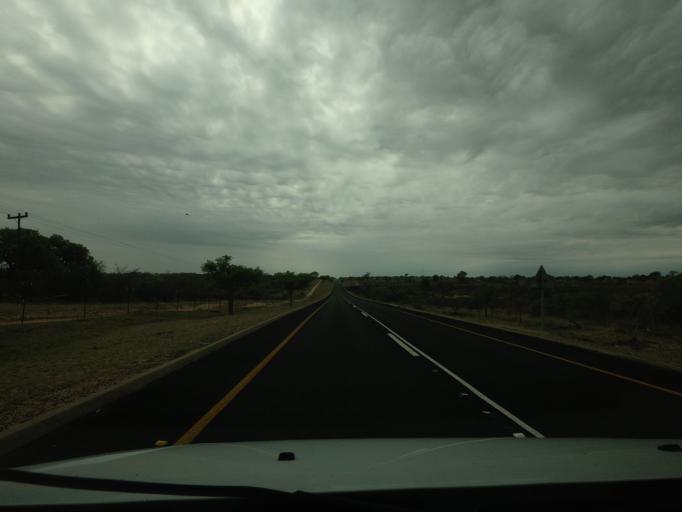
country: ZA
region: Limpopo
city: Thulamahashi
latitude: -24.5639
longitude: 31.1322
